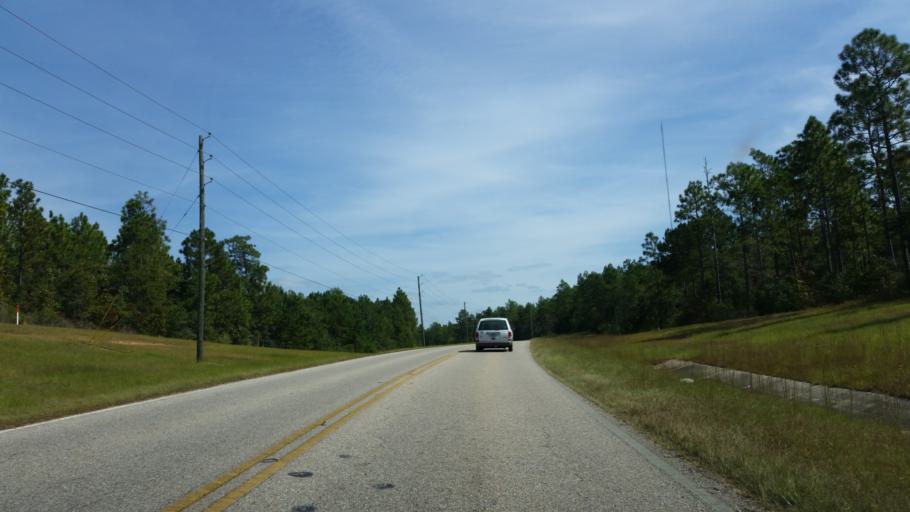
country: US
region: Alabama
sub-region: Baldwin County
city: Spanish Fort
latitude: 30.6860
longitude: -87.8503
